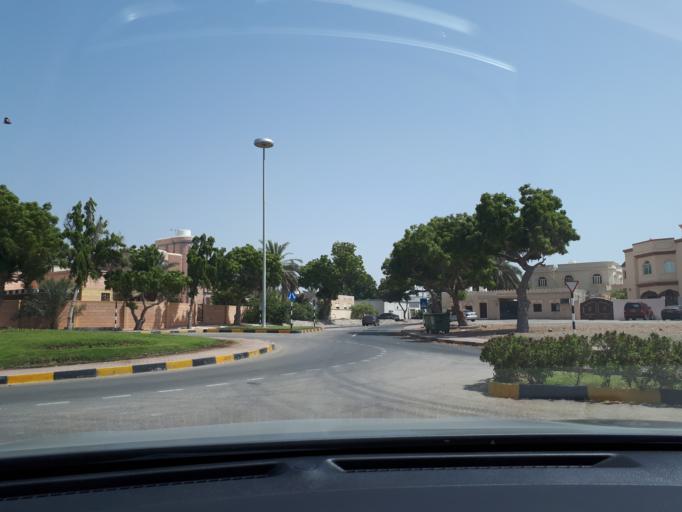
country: OM
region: Muhafazat Masqat
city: As Sib al Jadidah
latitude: 23.7100
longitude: 58.0745
